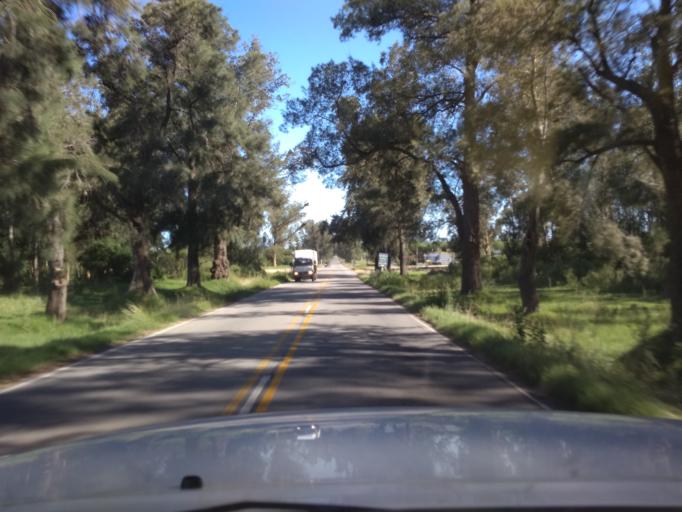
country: UY
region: Canelones
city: San Bautista
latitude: -34.3809
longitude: -55.9595
